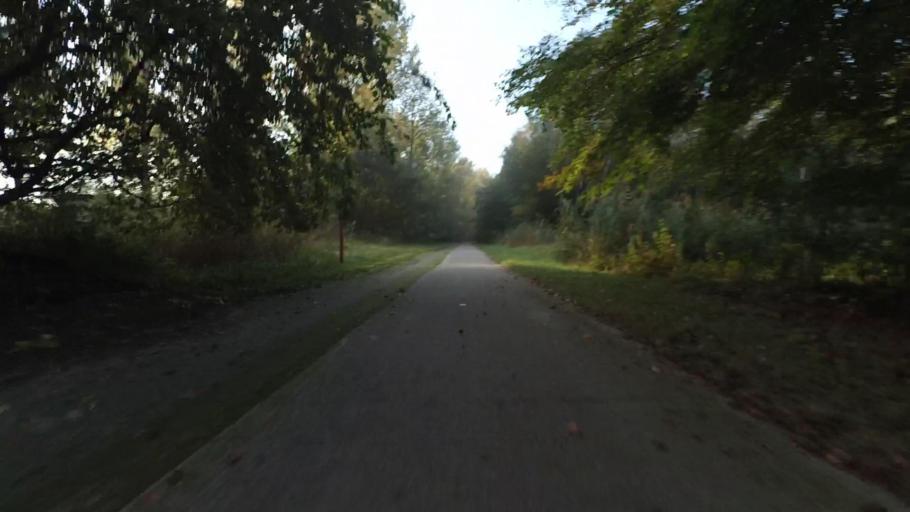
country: NL
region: Flevoland
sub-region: Gemeente Zeewolde
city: Zeewolde
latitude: 52.2800
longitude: 5.5260
